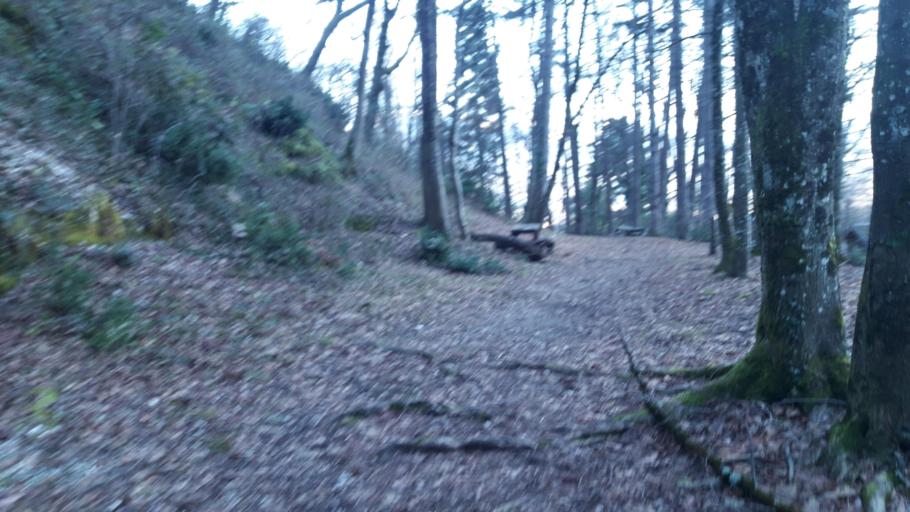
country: FR
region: Rhone-Alpes
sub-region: Departement de l'Isere
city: Seyssins
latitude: 45.1725
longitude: 5.6731
